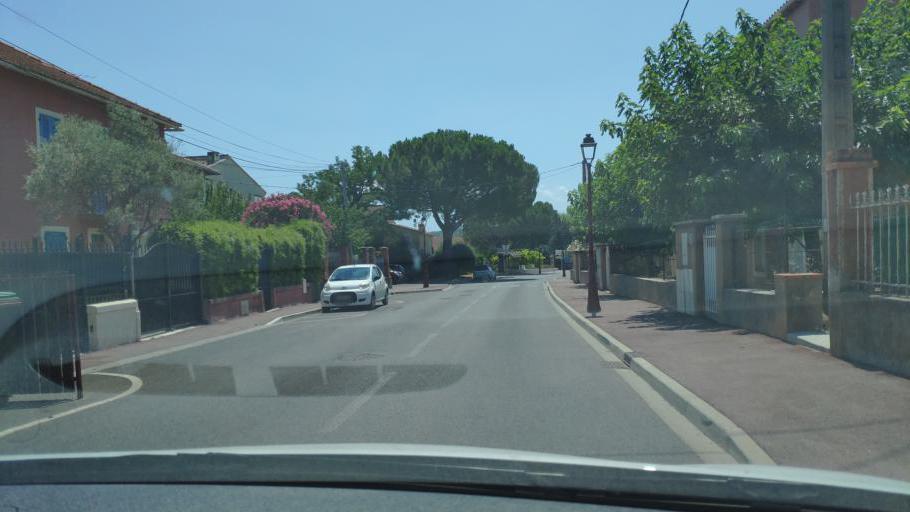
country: FR
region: Provence-Alpes-Cote d'Azur
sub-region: Departement du Var
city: Les Arcs
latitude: 43.4581
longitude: 6.4807
